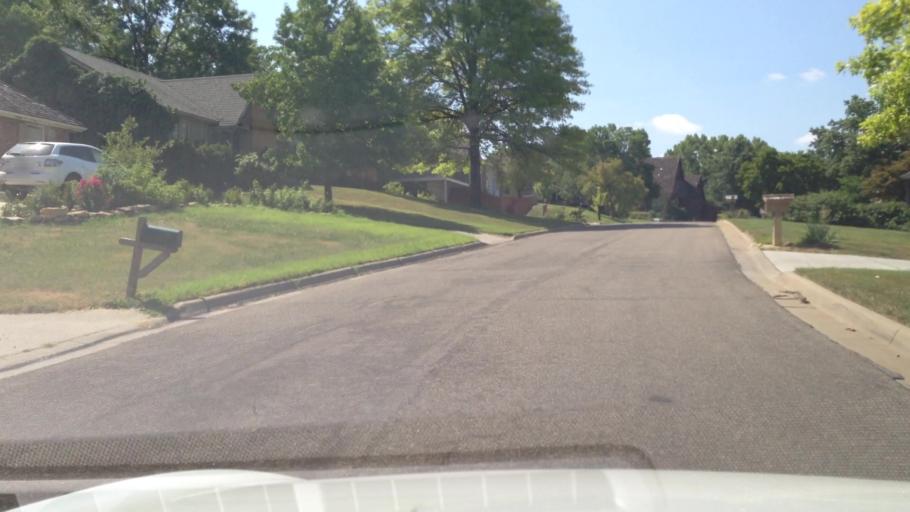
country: US
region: Kansas
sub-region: Douglas County
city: Lawrence
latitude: 38.9490
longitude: -95.2810
